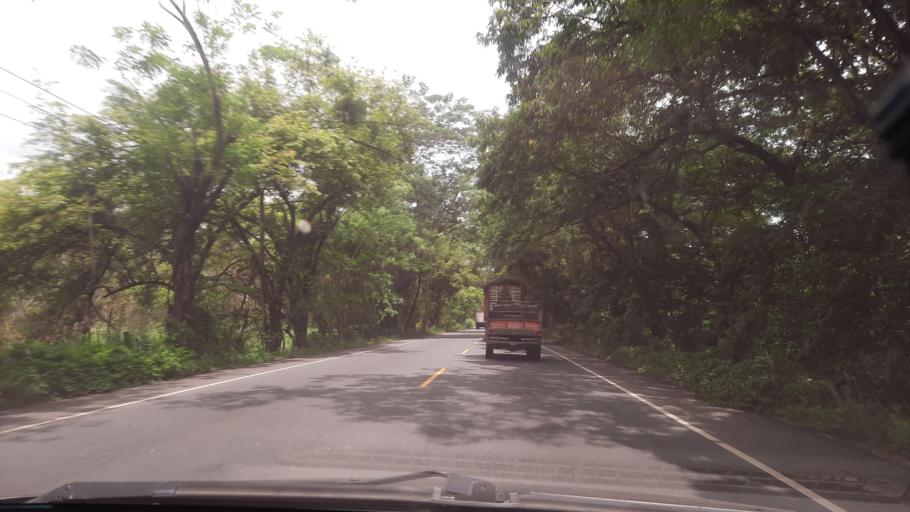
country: GT
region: Zacapa
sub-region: Municipio de Zacapa
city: Gualan
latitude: 15.1986
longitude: -89.2629
